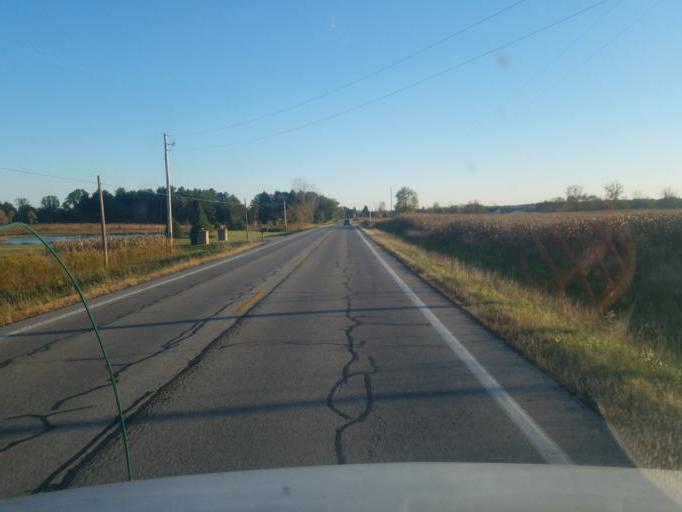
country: US
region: Ohio
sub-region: Licking County
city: Utica
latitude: 40.3072
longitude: -82.4570
